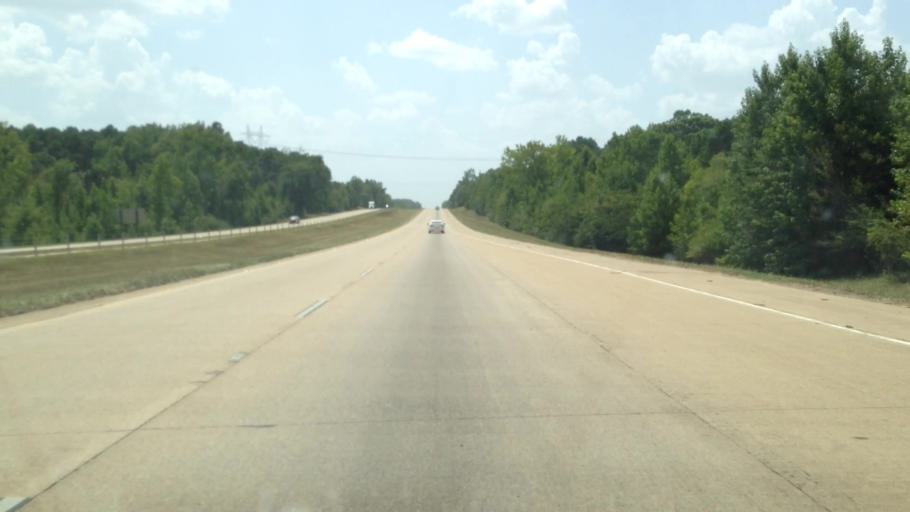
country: US
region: Louisiana
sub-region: Lincoln Parish
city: Grambling
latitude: 32.5423
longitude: -92.7187
